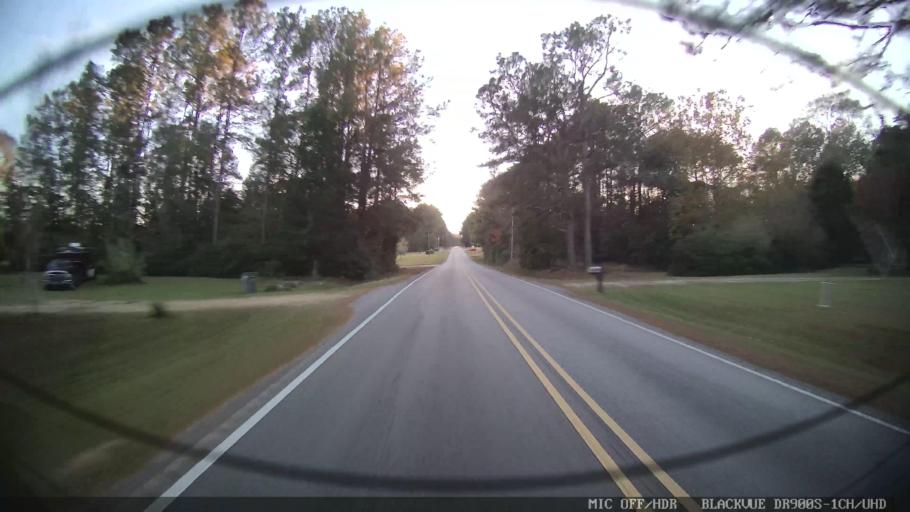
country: US
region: Mississippi
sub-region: Stone County
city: Wiggins
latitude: 31.0435
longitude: -89.2119
